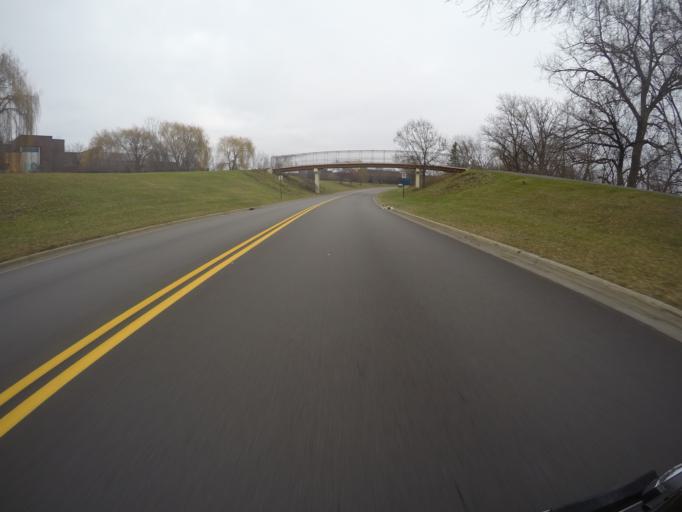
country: US
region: Minnesota
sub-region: Hennepin County
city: Eden Prairie
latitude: 44.8705
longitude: -93.4931
